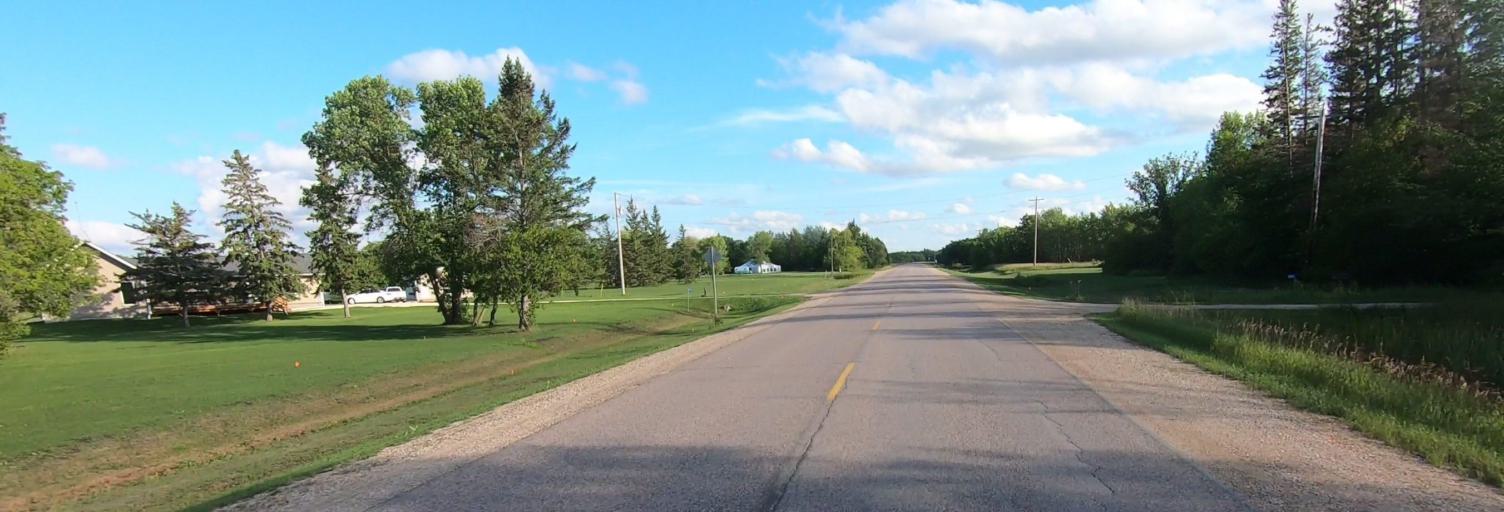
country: CA
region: Manitoba
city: Selkirk
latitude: 50.2102
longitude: -96.8411
